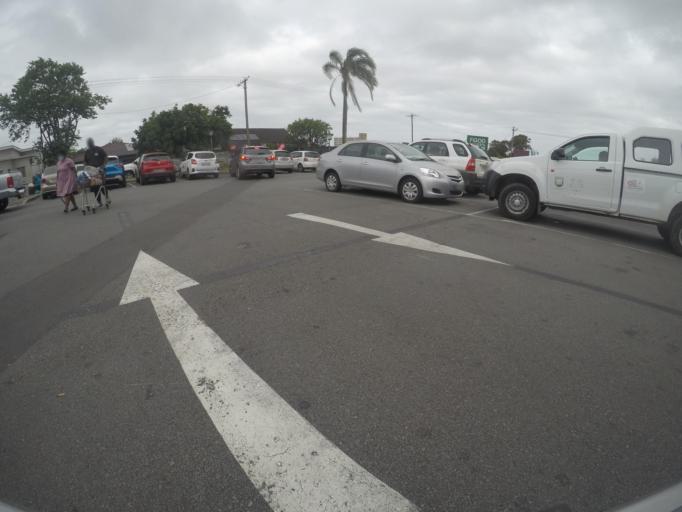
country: ZA
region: Eastern Cape
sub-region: Buffalo City Metropolitan Municipality
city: East London
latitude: -32.9807
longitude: 27.9011
